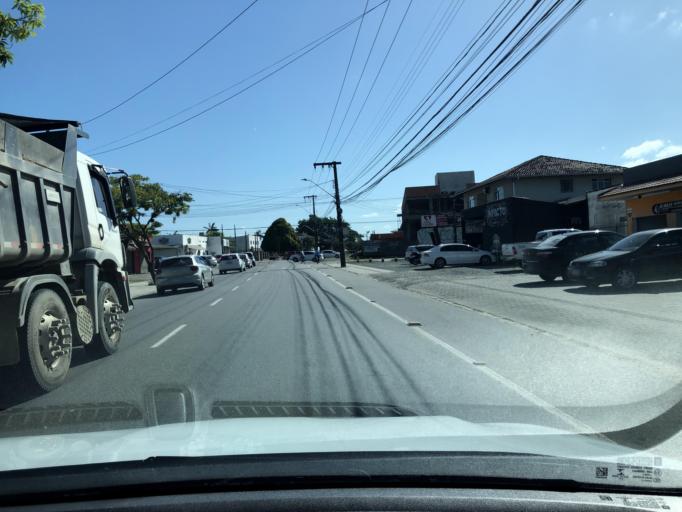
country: BR
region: Santa Catarina
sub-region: Joinville
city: Joinville
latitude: -26.3205
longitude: -48.8320
